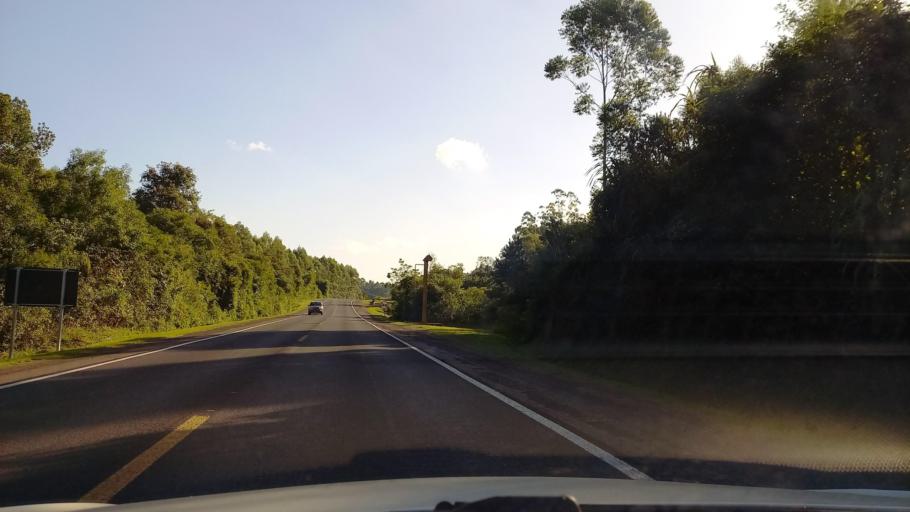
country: BR
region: Rio Grande do Sul
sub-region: Taquari
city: Taquari
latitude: -29.7113
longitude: -51.7716
